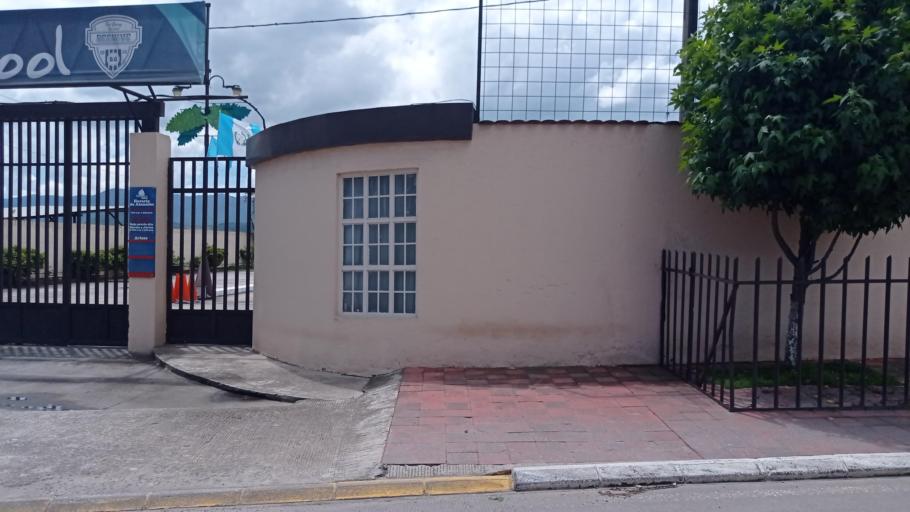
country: GT
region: Quetzaltenango
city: Olintepeque
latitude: 14.8680
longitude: -91.5056
